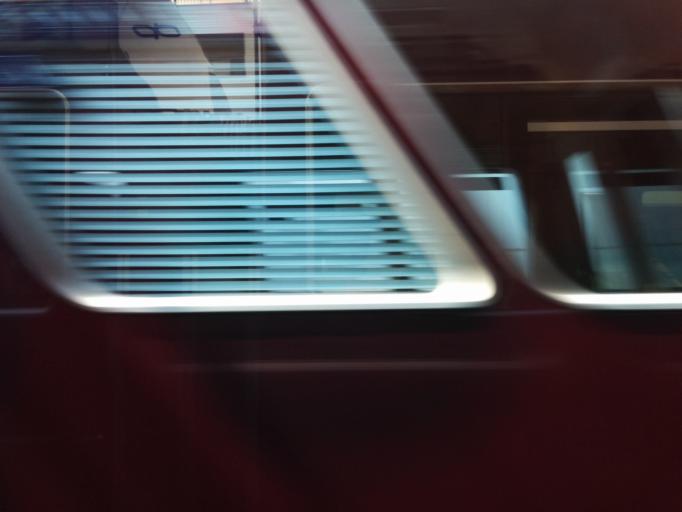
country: JP
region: Osaka
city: Suita
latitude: 34.7496
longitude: 135.5329
